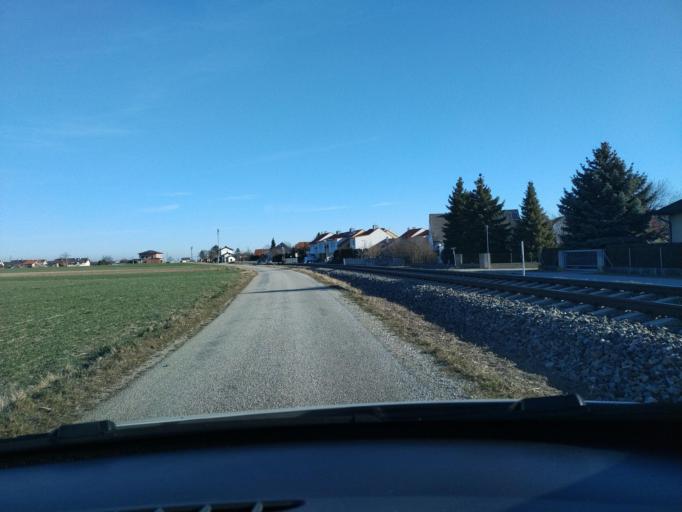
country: AT
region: Lower Austria
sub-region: Politischer Bezirk Wiener Neustadt
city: Lanzenkirchen
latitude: 47.7475
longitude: 16.2411
